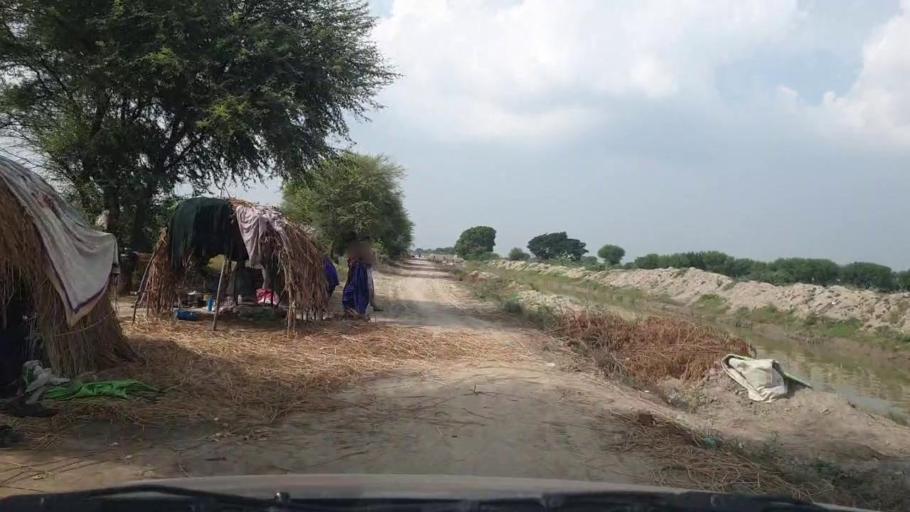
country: PK
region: Sindh
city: Badin
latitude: 24.5746
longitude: 68.6292
